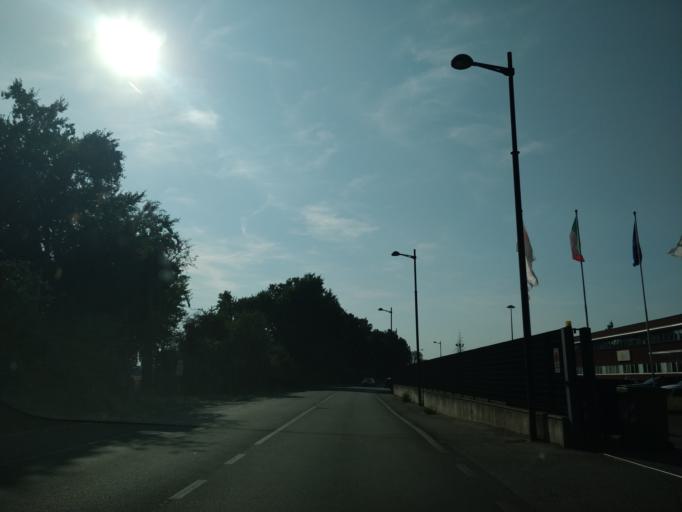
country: IT
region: Emilia-Romagna
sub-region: Provincia di Bologna
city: Progresso
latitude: 44.5598
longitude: 11.3528
